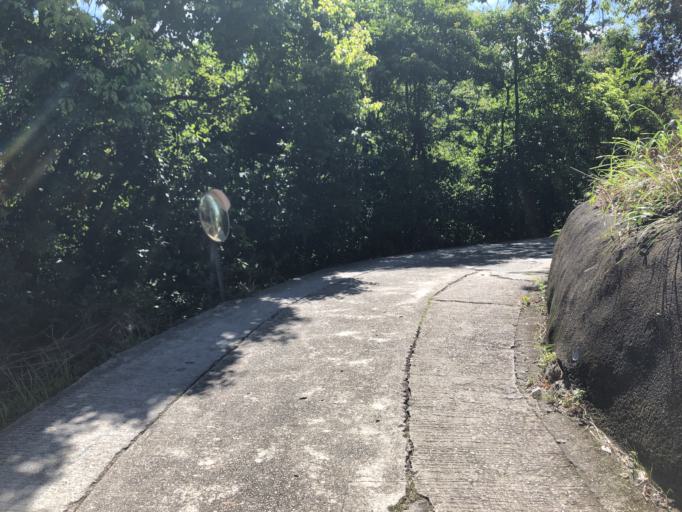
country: HK
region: Tuen Mun
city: Tuen Mun
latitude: 22.2934
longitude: 113.9748
